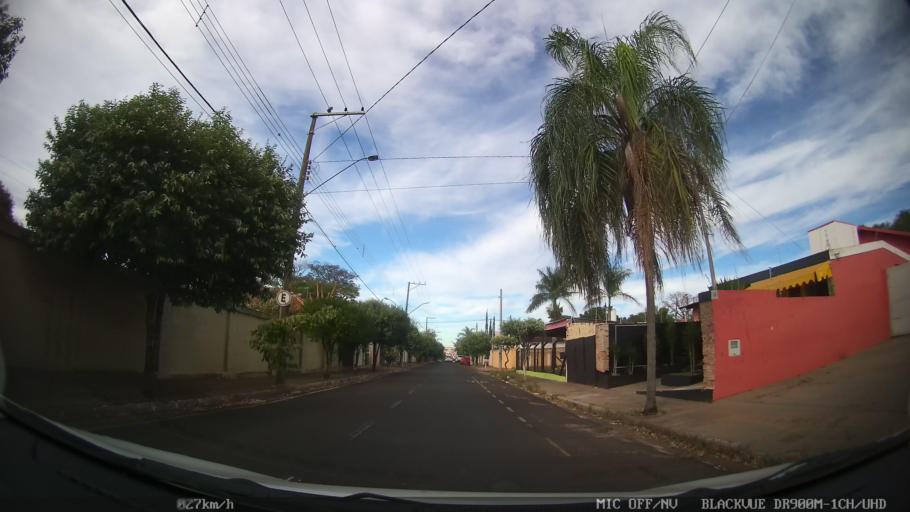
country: BR
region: Sao Paulo
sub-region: Catanduva
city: Catanduva
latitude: -21.1235
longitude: -48.9662
